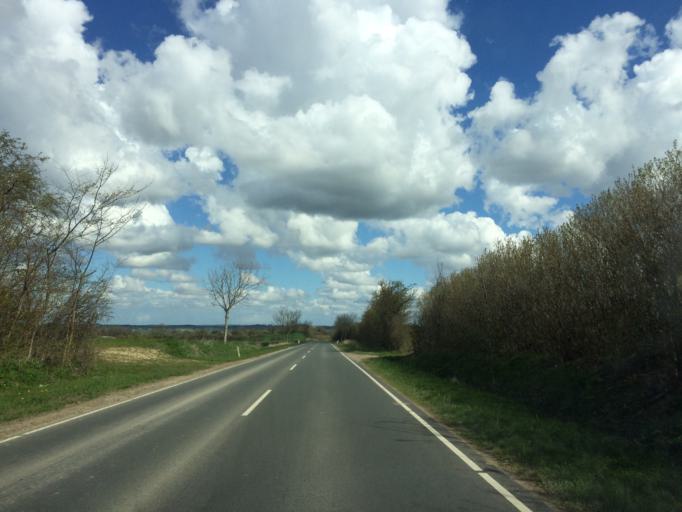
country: DK
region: South Denmark
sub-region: Assens Kommune
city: Harby
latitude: 55.2095
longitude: 10.1594
